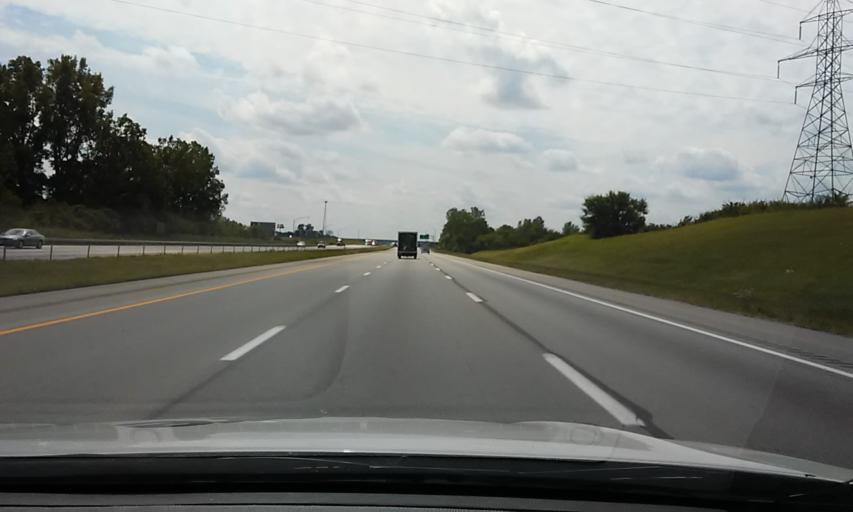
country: US
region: Ohio
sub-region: Clark County
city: Lisbon
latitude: 39.9032
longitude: -83.7167
